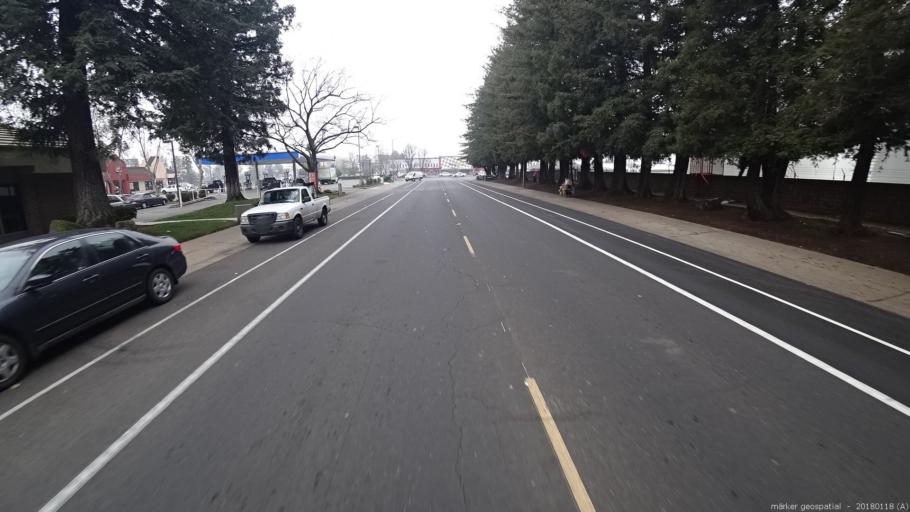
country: US
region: California
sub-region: Sacramento County
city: La Riviera
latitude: 38.5689
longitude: -121.3351
